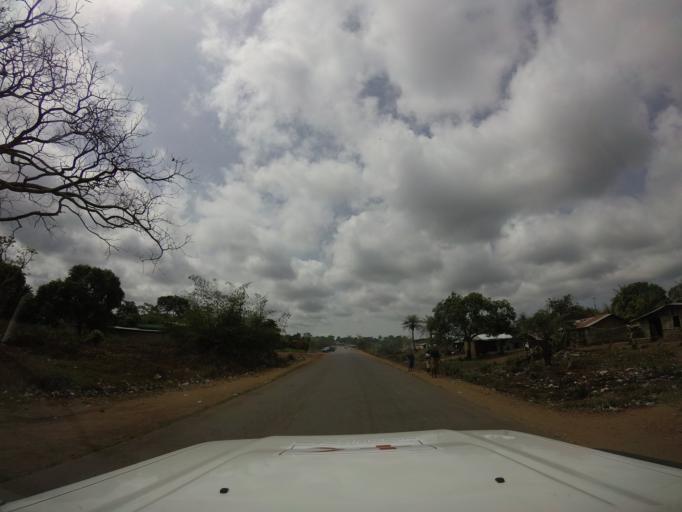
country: LR
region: Montserrado
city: Monrovia
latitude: 6.4843
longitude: -10.8134
